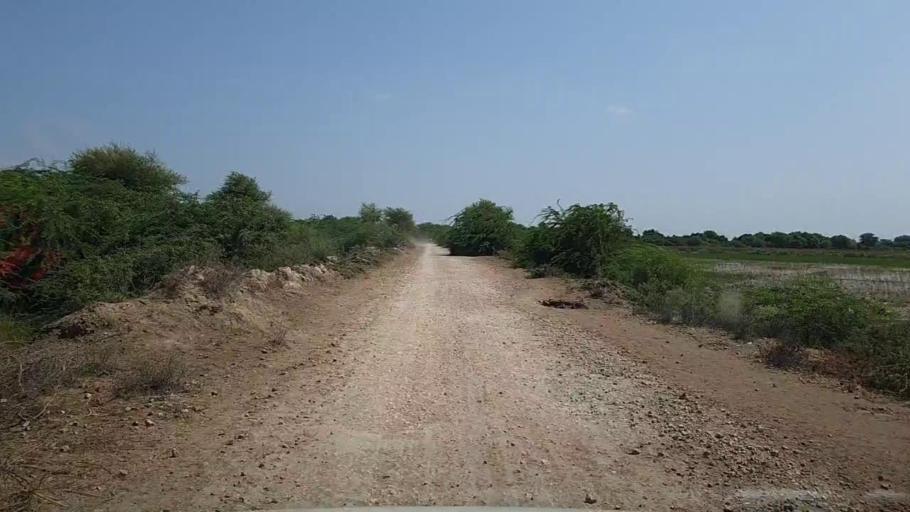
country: PK
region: Sindh
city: Kario
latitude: 24.8382
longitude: 68.7073
